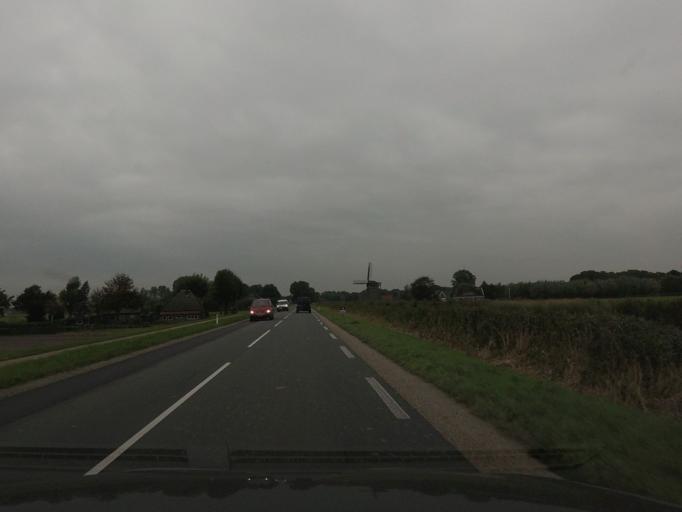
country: NL
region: North Holland
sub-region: Gemeente Heerhugowaard
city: Heerhugowaard
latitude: 52.7173
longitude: 4.8689
